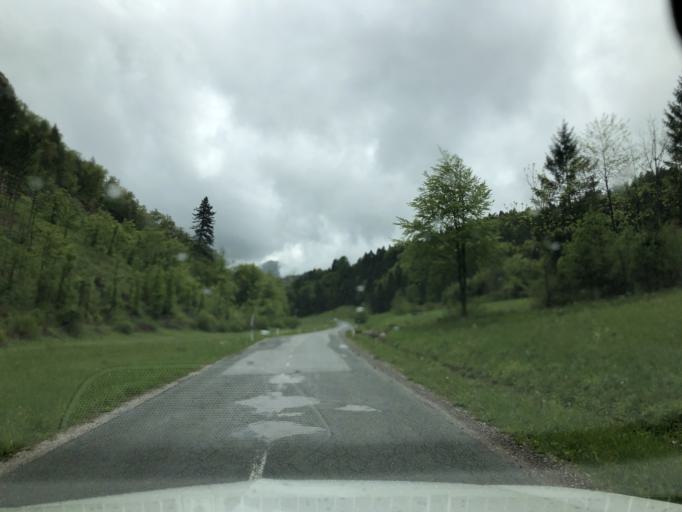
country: SI
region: Gorje
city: Zgornje Gorje
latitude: 46.4022
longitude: 14.0767
